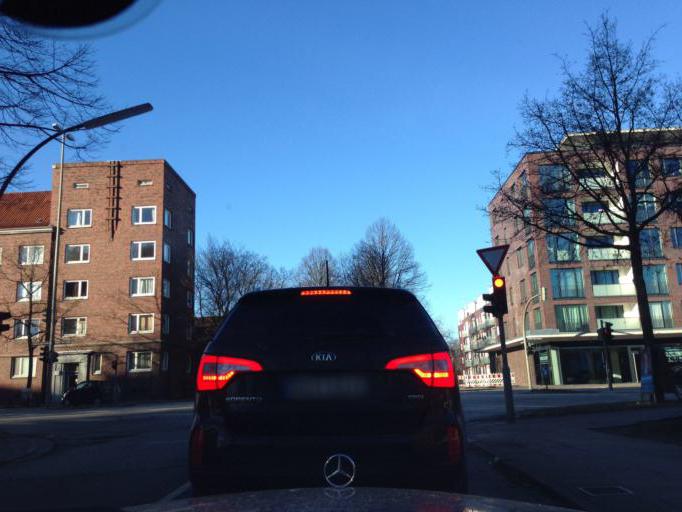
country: DE
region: Hamburg
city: Marienthal
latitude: 53.5859
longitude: 10.0856
